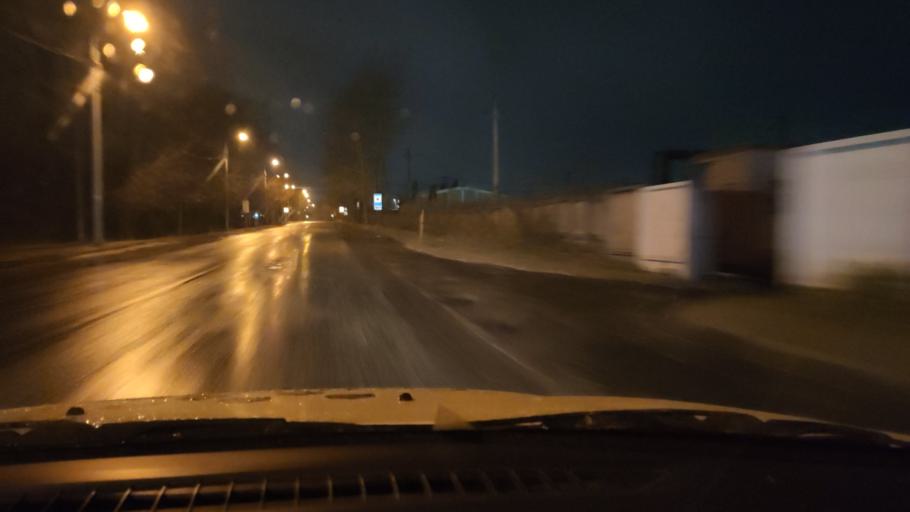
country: RU
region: Perm
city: Kondratovo
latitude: 58.0033
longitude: 56.1721
